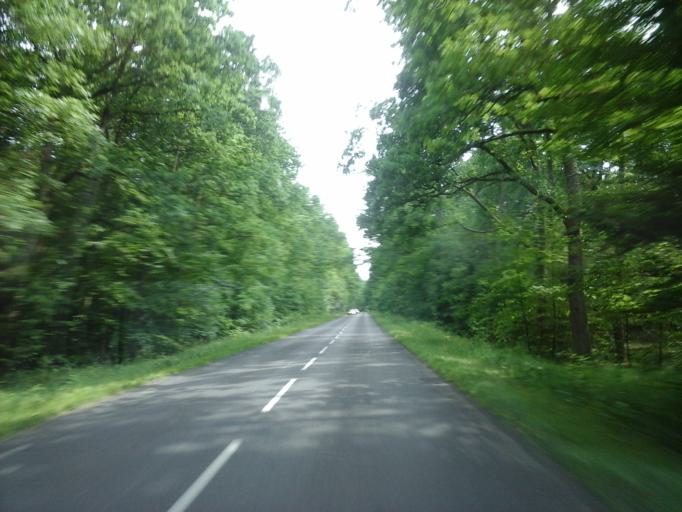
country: PL
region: West Pomeranian Voivodeship
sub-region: Powiat lobeski
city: Lobez
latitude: 53.6108
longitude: 15.6130
